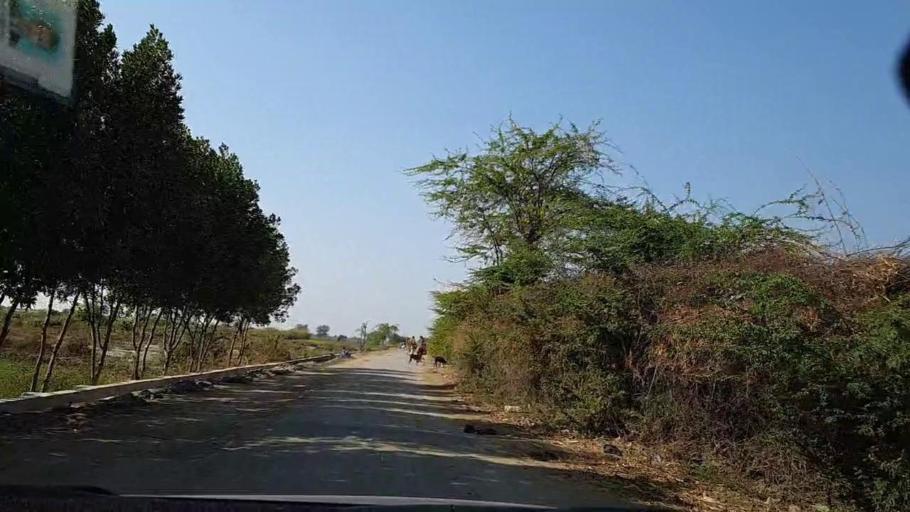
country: PK
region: Sindh
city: Digri
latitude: 25.1653
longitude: 69.0687
